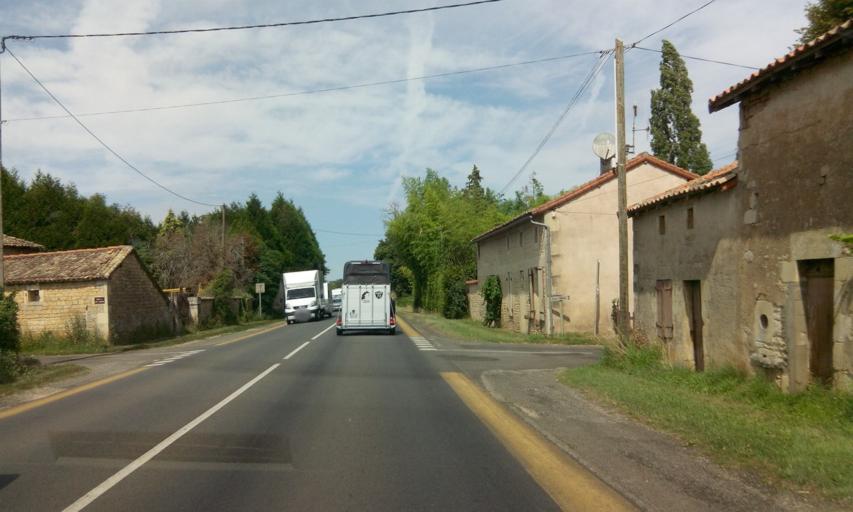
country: FR
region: Poitou-Charentes
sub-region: Departement des Deux-Sevres
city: Sauze-Vaussais
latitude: 46.1547
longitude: 0.0509
